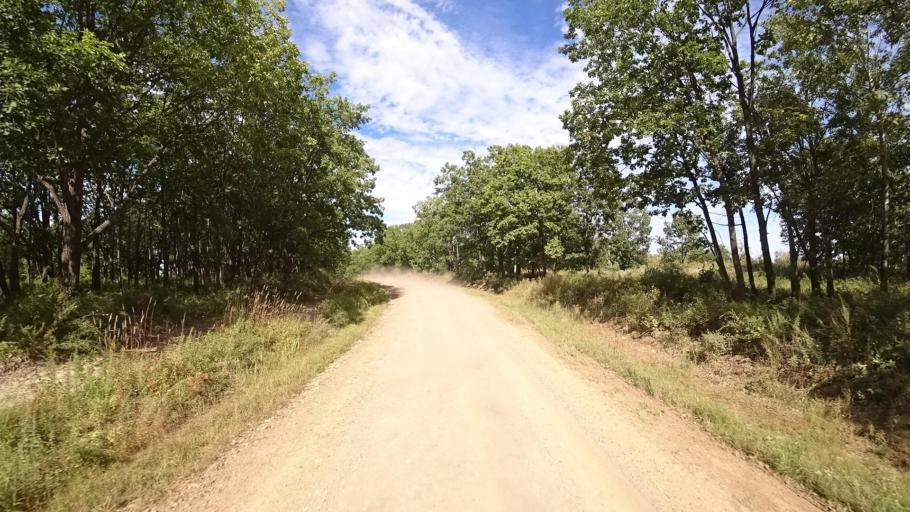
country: RU
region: Primorskiy
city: Yakovlevka
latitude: 44.4026
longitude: 133.5652
